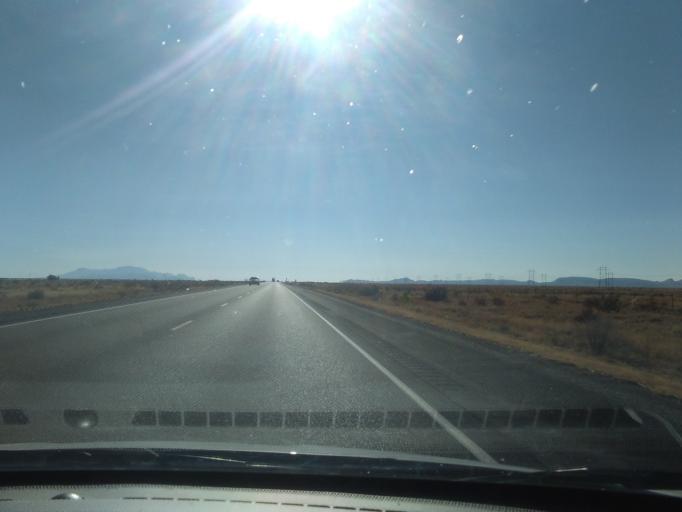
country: US
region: New Mexico
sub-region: Dona Ana County
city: Hatch
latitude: 32.5360
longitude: -107.4861
